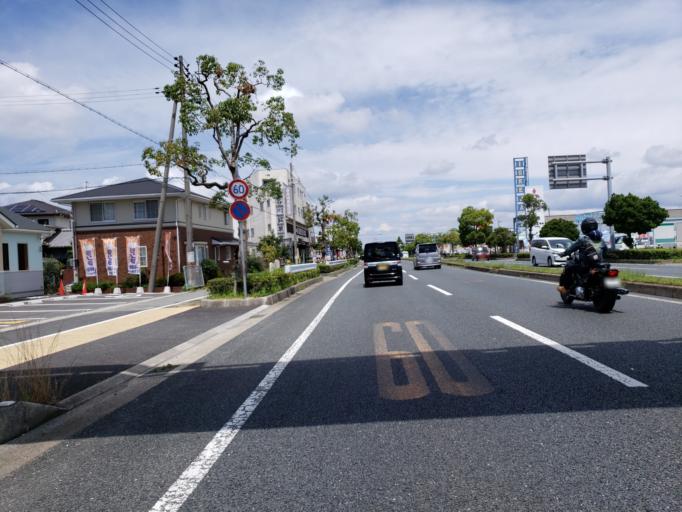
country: JP
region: Hyogo
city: Kakogawacho-honmachi
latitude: 34.7256
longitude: 134.8659
